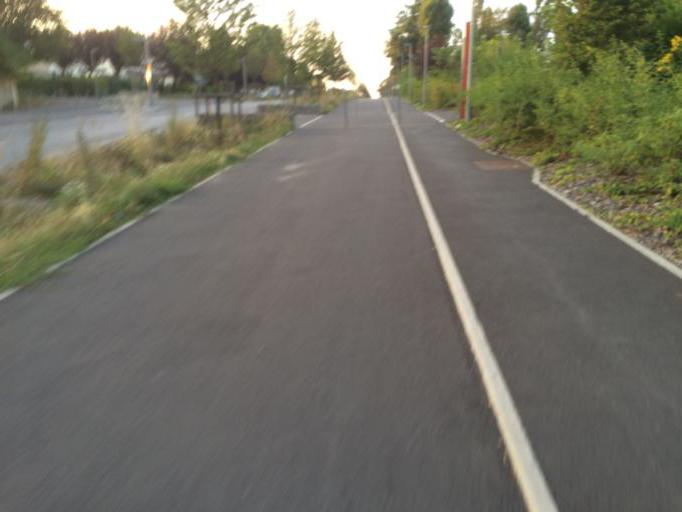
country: FR
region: Ile-de-France
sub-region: Departement de l'Essonne
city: Longjumeau
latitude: 48.7060
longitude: 2.2972
